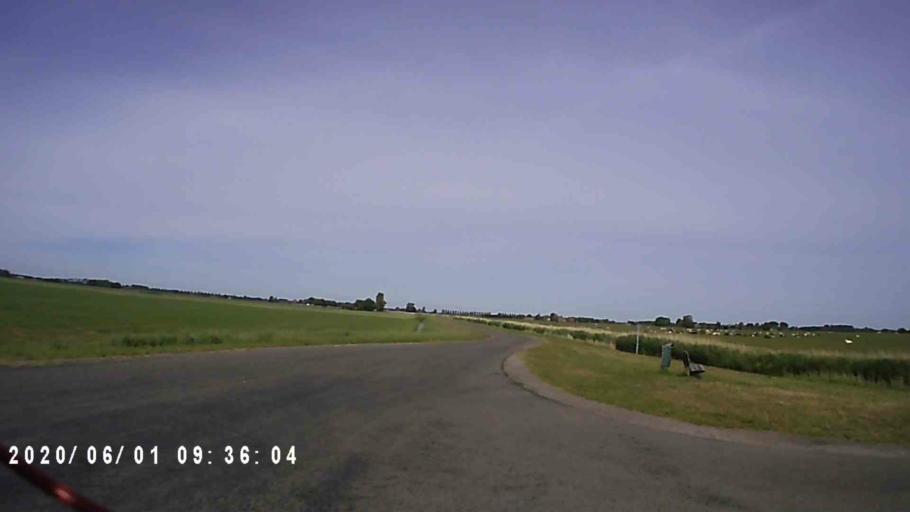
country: NL
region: Friesland
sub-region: Gemeente Het Bildt
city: Sint Annaparochie
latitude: 53.2597
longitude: 5.7003
